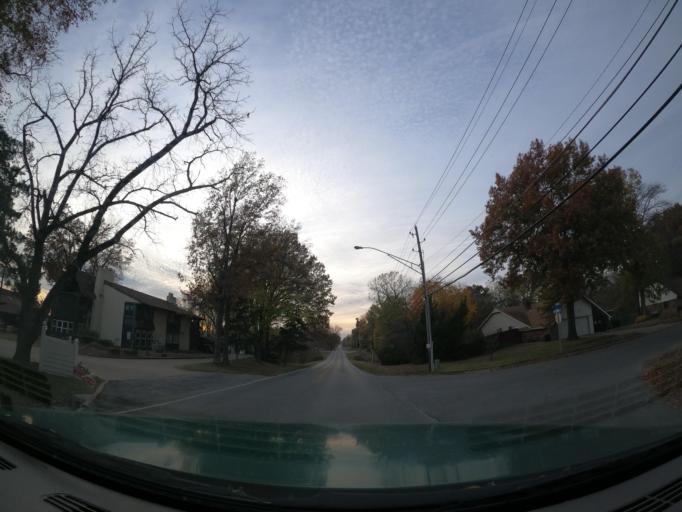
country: US
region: Oklahoma
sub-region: Tulsa County
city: Broken Arrow
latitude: 35.9738
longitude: -95.8010
